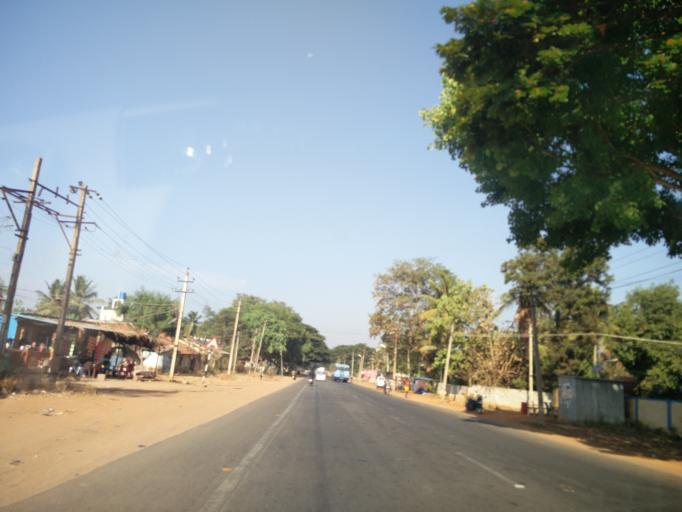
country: IN
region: Karnataka
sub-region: Tumkur
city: Gubbi
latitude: 13.3108
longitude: 76.9520
